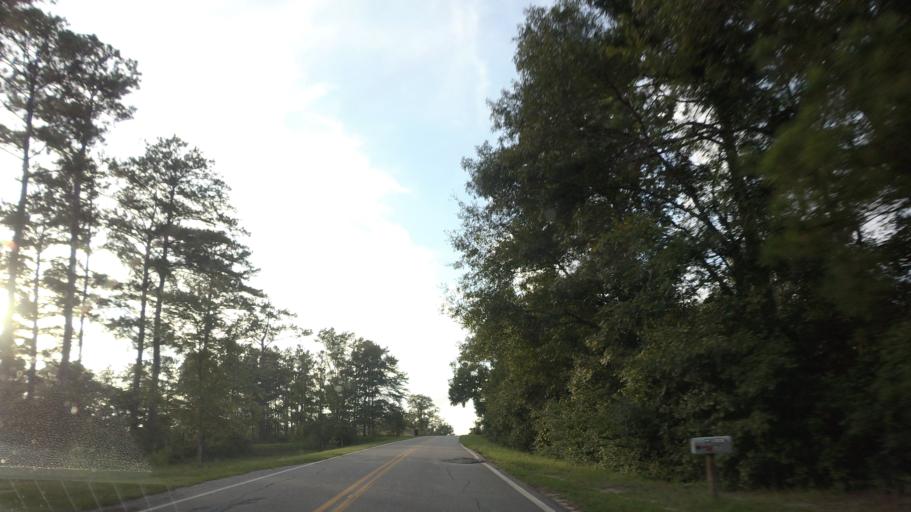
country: US
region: Georgia
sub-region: Wilkinson County
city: Gordon
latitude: 32.8421
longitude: -83.4153
